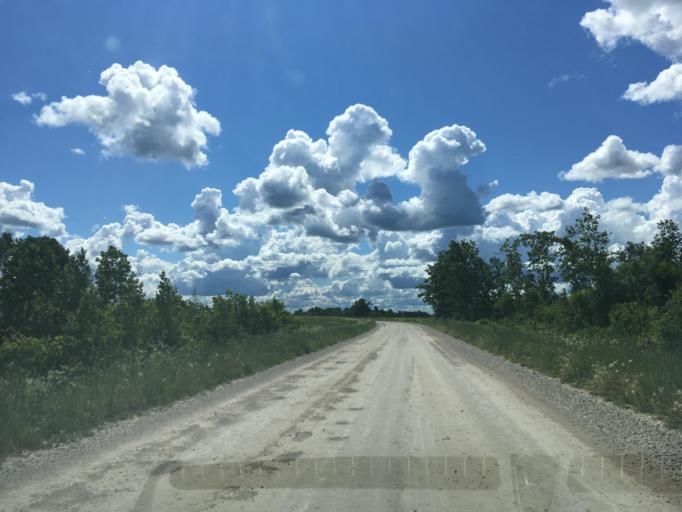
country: EE
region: Harju
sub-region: Nissi vald
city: Turba
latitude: 58.9299
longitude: 24.1528
